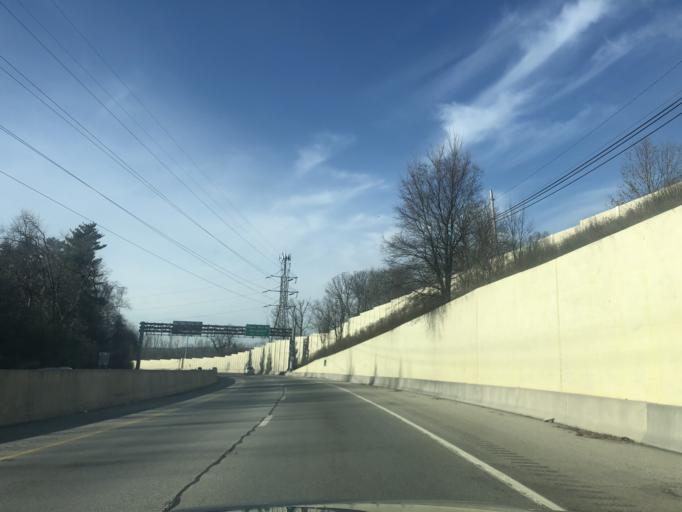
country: US
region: Pennsylvania
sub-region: Montgomery County
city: Oreland
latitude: 40.0992
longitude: -75.1797
